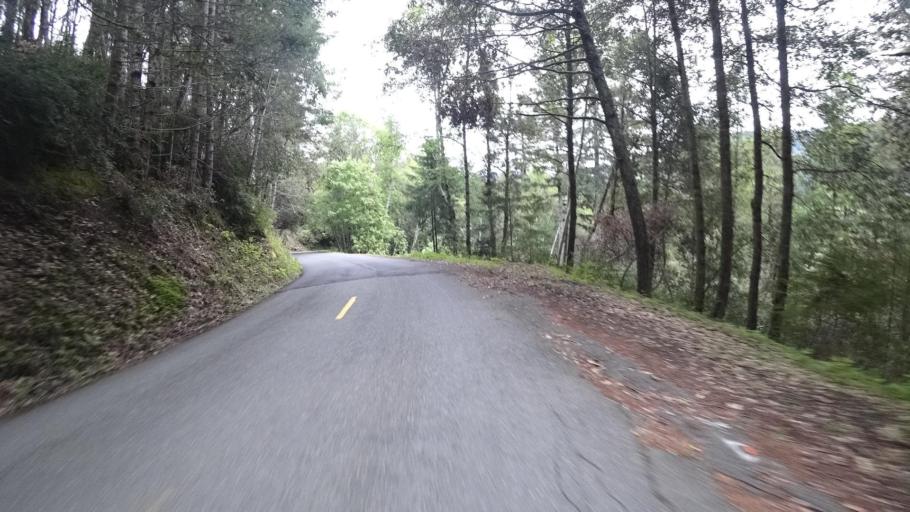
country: US
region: California
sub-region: Humboldt County
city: Blue Lake
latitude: 40.9392
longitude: -123.8427
